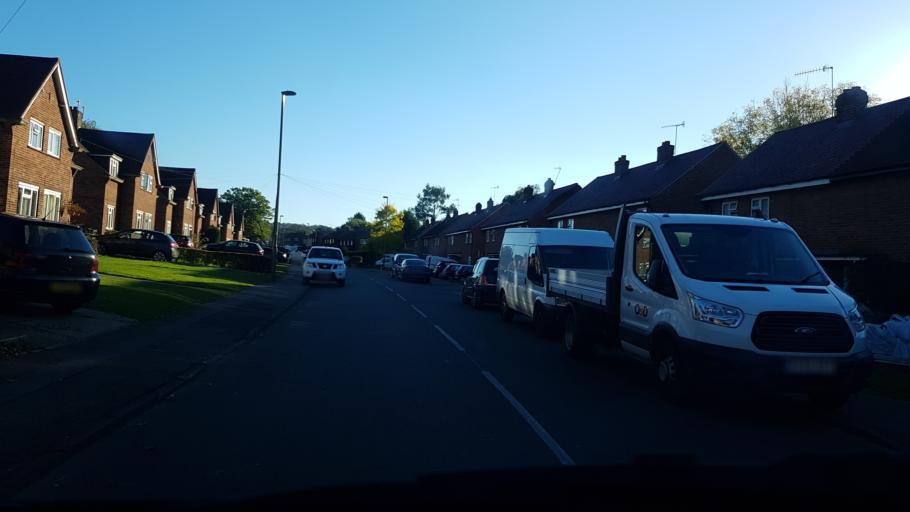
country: GB
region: England
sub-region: Surrey
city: Guildford
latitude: 51.2482
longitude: -0.6116
